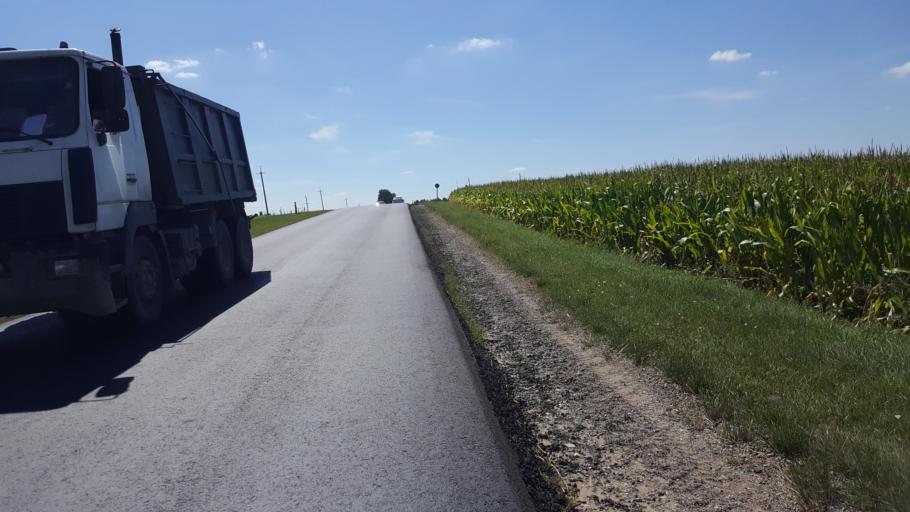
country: BY
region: Brest
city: Charnawchytsy
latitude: 52.2896
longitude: 23.6051
